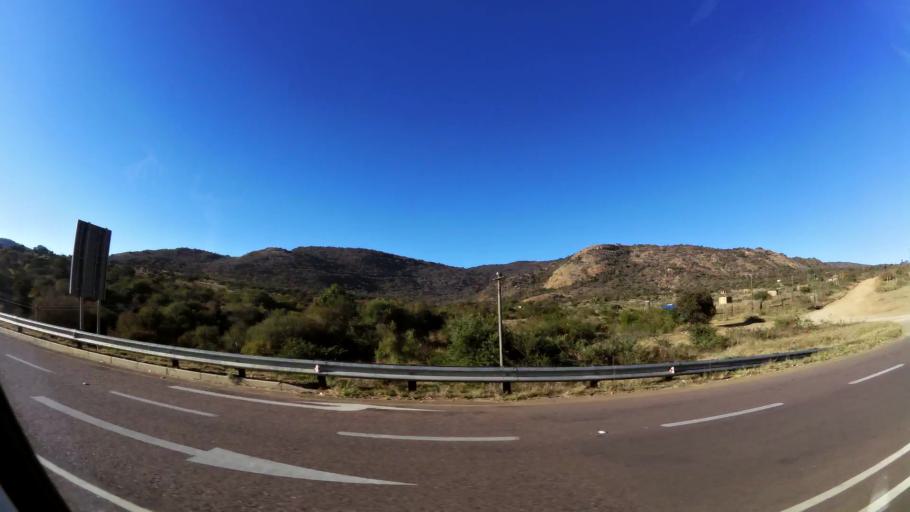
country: ZA
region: Limpopo
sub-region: Capricorn District Municipality
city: Mankoeng
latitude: -23.9266
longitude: 29.8667
